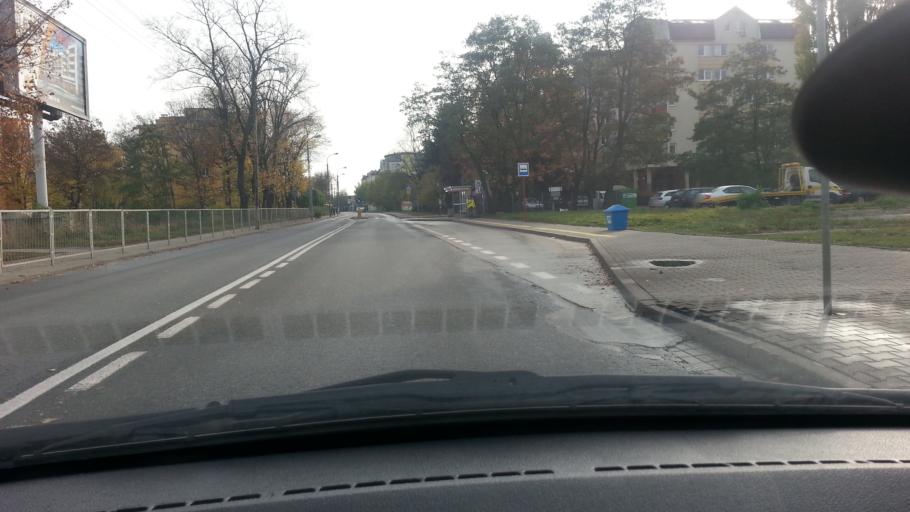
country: PL
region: Masovian Voivodeship
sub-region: Warszawa
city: Ursus
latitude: 52.1952
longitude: 20.8991
